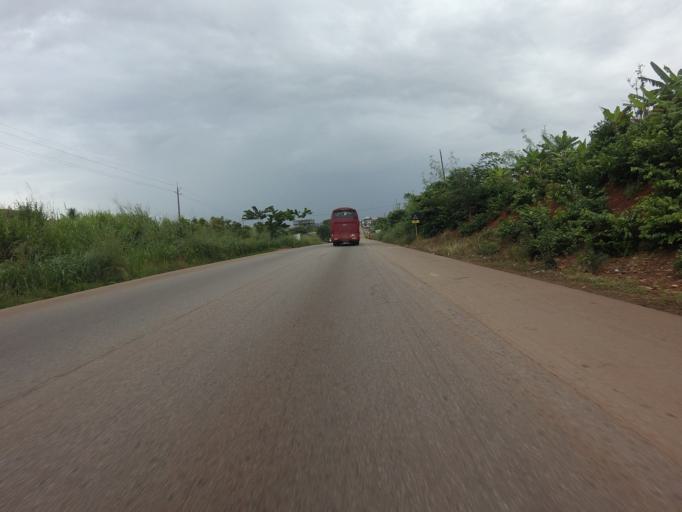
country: GH
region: Ashanti
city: Konongo
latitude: 6.6182
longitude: -1.1899
